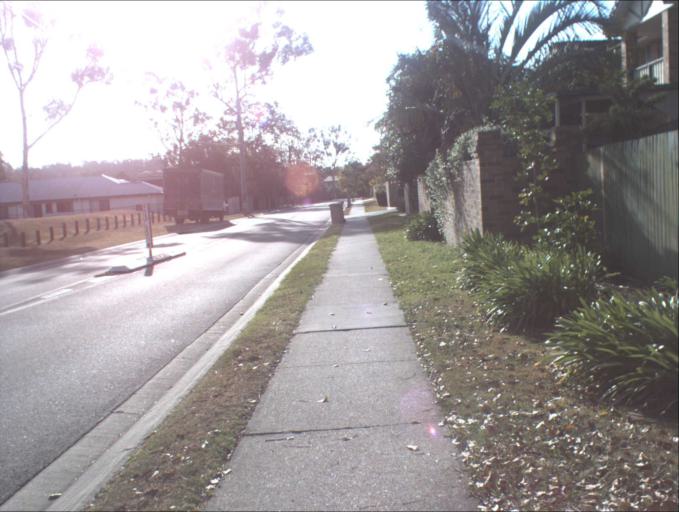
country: AU
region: Queensland
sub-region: Logan
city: Slacks Creek
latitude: -27.6623
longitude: 153.1796
